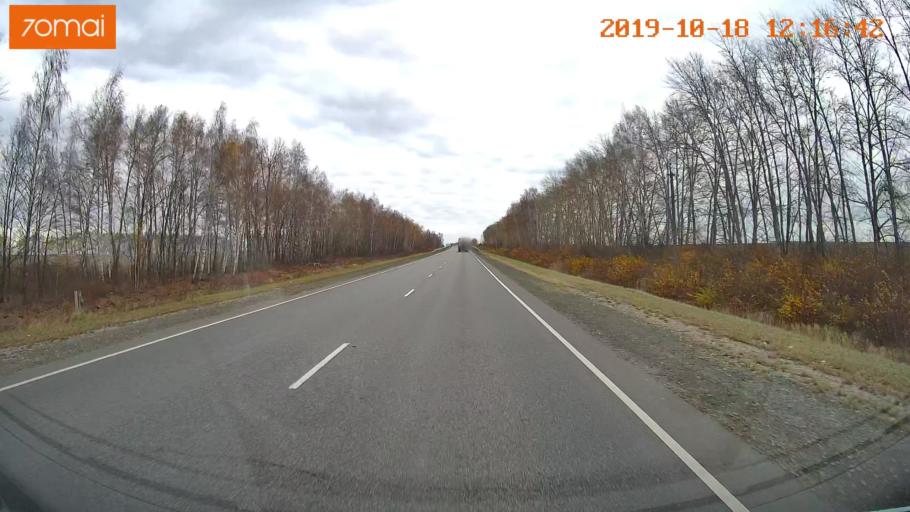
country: RU
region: Rjazan
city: Zakharovo
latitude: 54.4535
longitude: 39.4276
